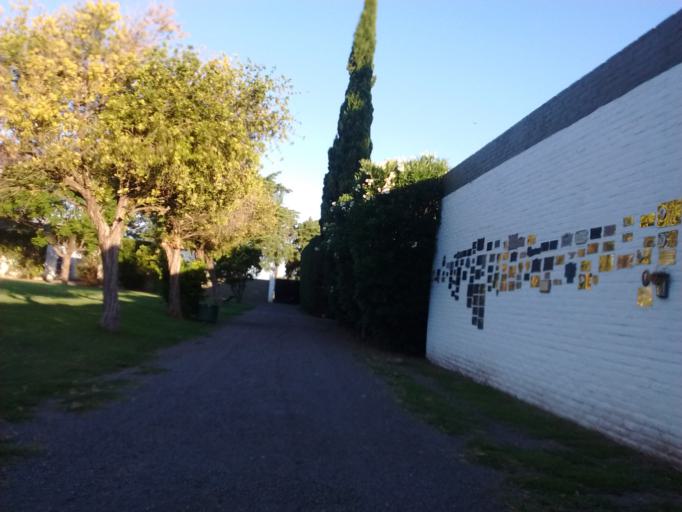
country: AR
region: Santa Fe
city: Funes
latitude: -32.9195
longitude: -60.7911
